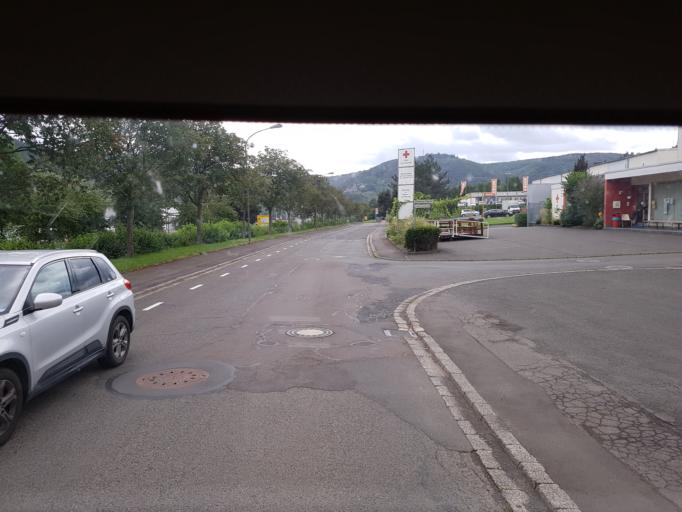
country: DE
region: Rheinland-Pfalz
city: Bernkastel-Kues
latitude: 49.9282
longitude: 7.0600
